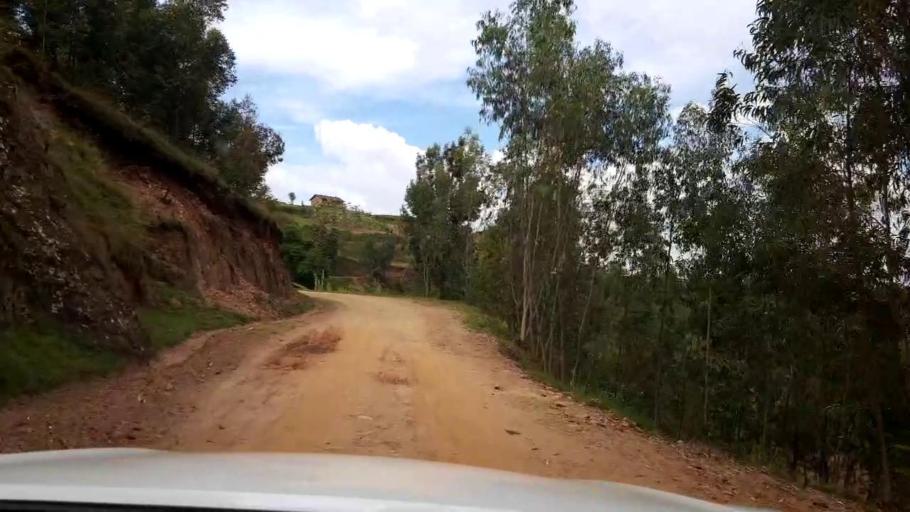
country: RW
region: Southern Province
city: Gitarama
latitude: -1.9868
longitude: 29.7073
